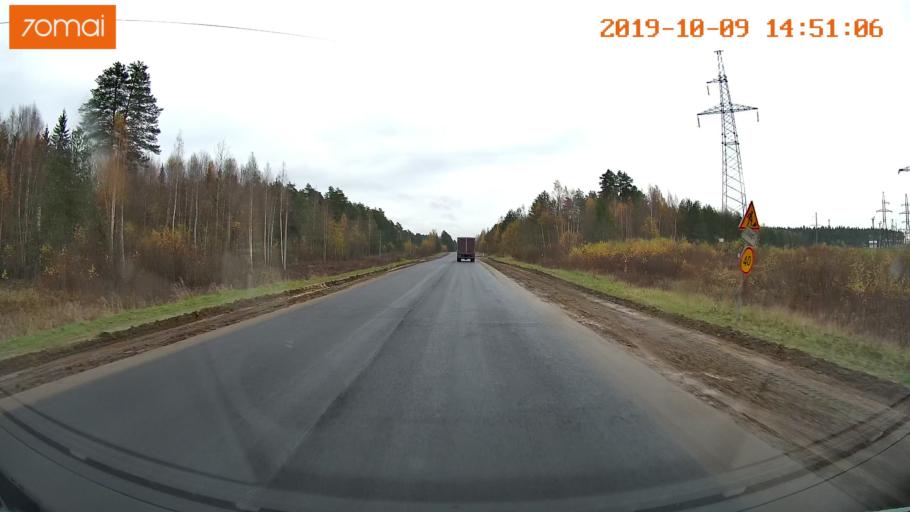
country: RU
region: Kostroma
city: Chistyye Bory
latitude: 58.3793
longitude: 41.6107
